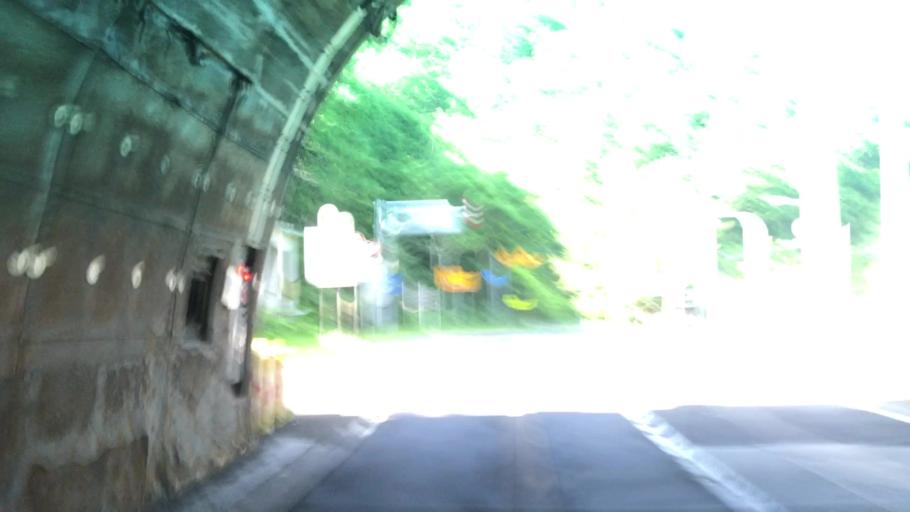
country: JP
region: Hokkaido
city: Yoichi
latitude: 43.0606
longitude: 140.6863
